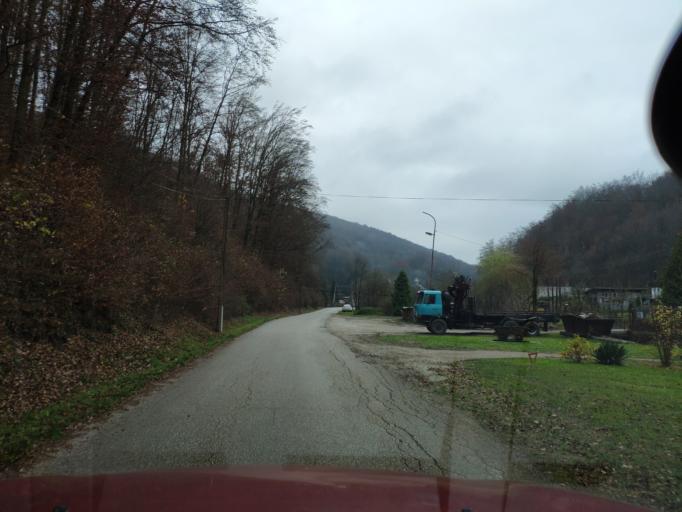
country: SK
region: Kosicky
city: Roznava
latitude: 48.6995
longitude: 20.5469
